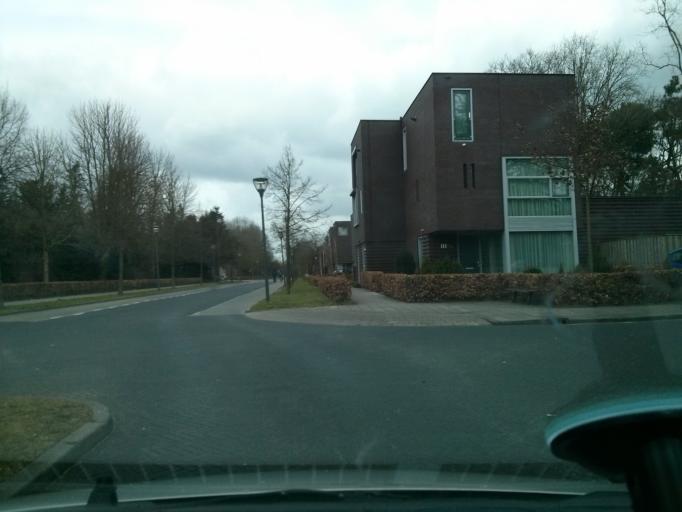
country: NL
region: North Brabant
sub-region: Gemeente Son en Breugel
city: Son
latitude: 51.5148
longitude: 5.4934
